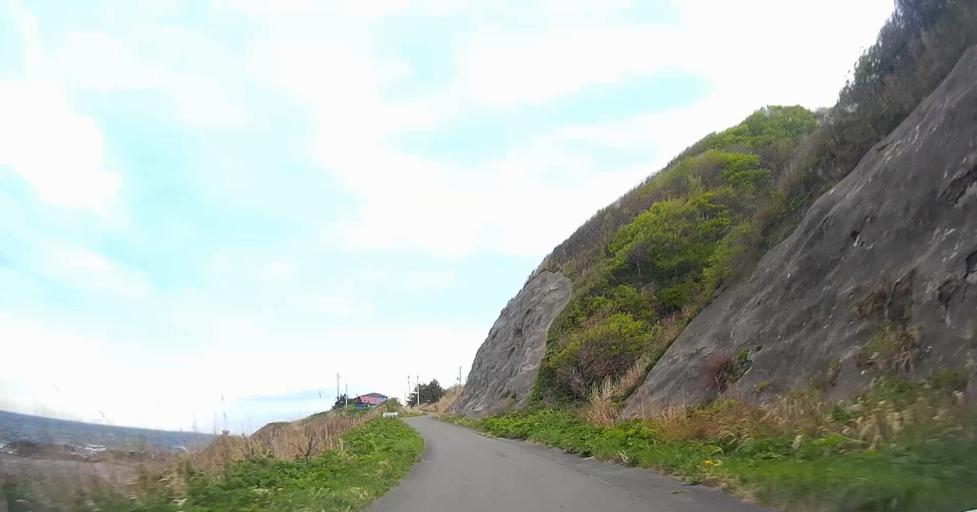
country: JP
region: Aomori
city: Shimokizukuri
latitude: 41.2420
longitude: 140.3426
